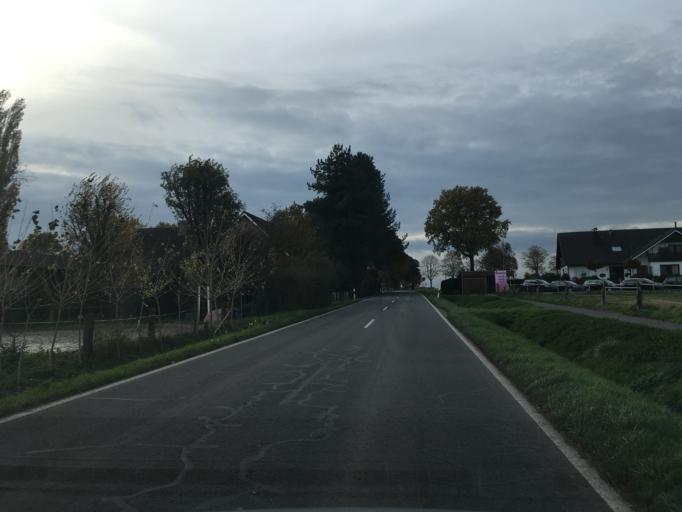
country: DE
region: North Rhine-Westphalia
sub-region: Regierungsbezirk Munster
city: Raesfeld
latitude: 51.7406
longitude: 6.8475
